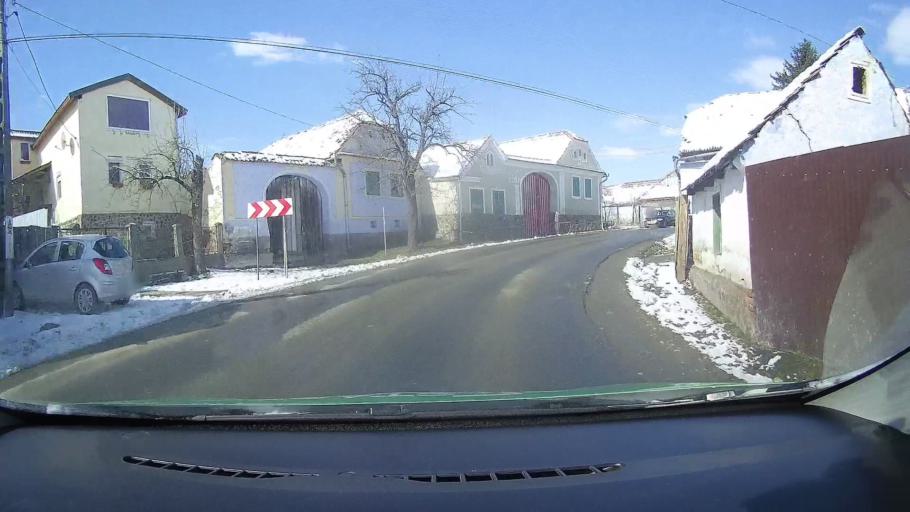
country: RO
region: Sibiu
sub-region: Comuna Barghis
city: Barghis
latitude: 45.9880
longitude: 24.4834
